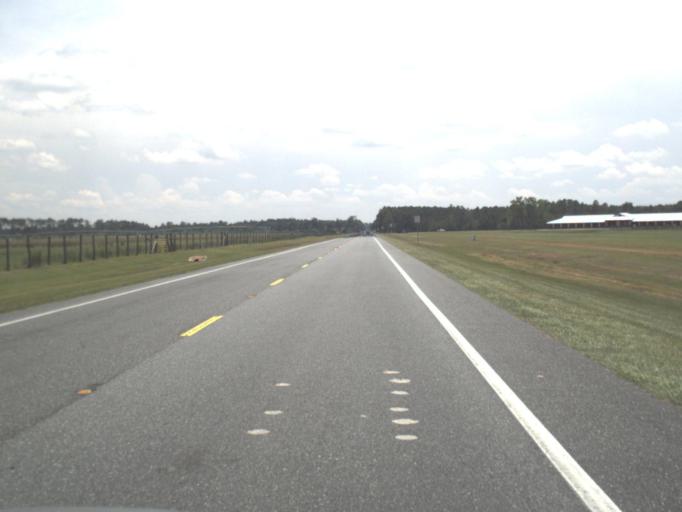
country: US
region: Florida
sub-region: Bradford County
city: Starke
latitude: 30.0526
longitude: -82.1744
